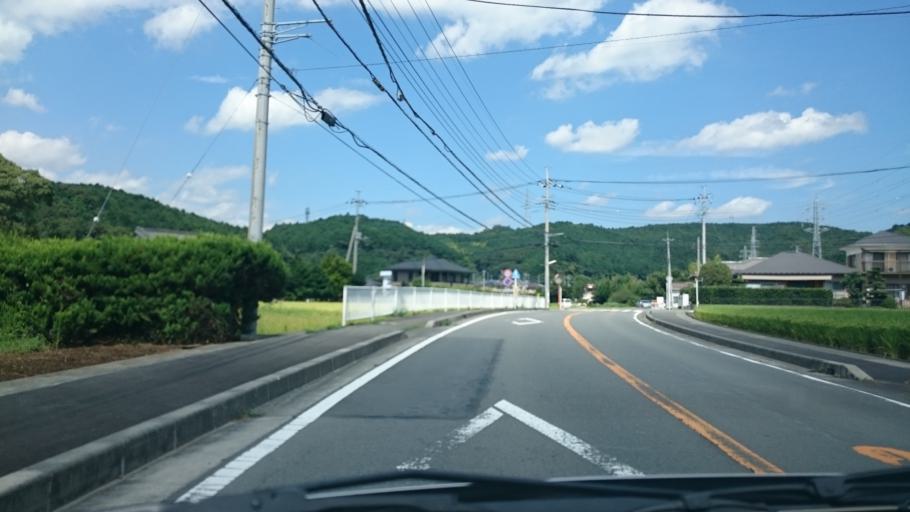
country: JP
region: Shizuoka
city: Gotemba
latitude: 35.2124
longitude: 138.9245
